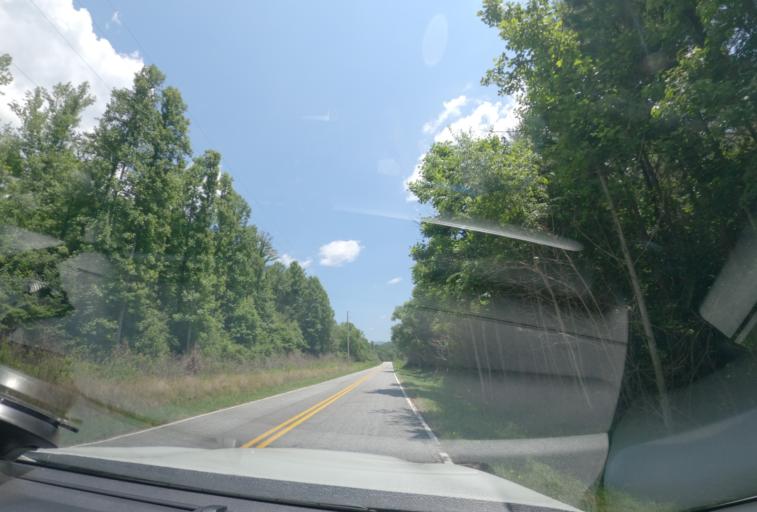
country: US
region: South Carolina
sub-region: Pickens County
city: Pickens
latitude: 34.9750
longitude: -82.8558
